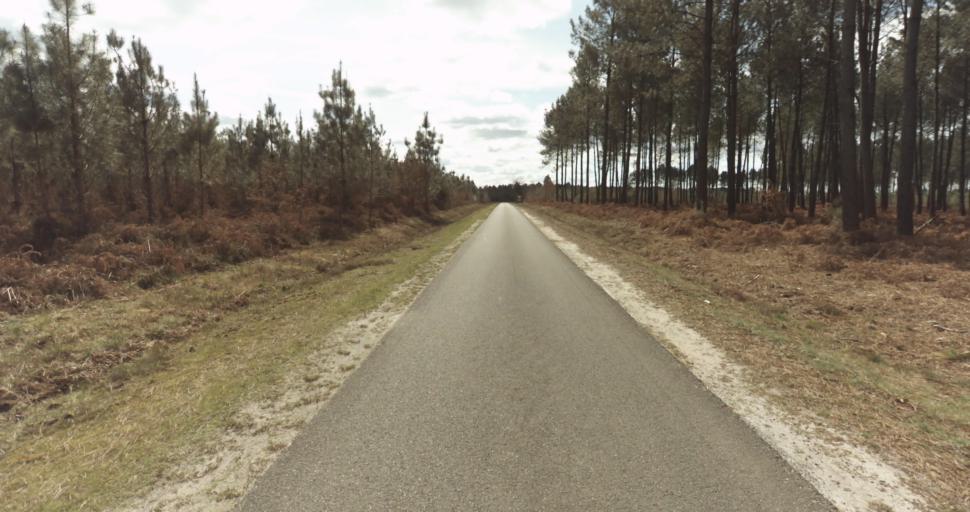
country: FR
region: Aquitaine
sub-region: Departement des Landes
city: Roquefort
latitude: 44.0362
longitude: -0.4229
